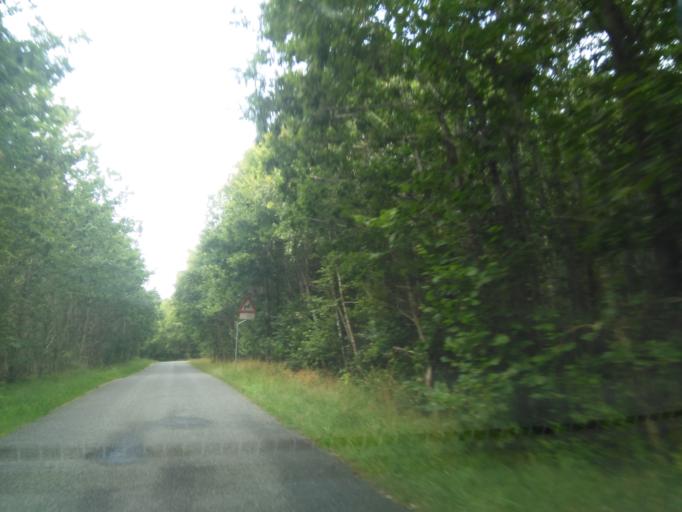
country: DK
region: Central Jutland
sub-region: Odder Kommune
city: Odder
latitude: 55.8847
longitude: 10.0502
